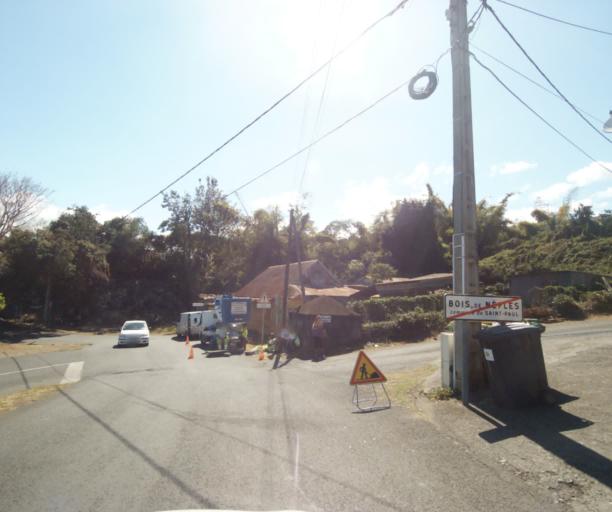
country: RE
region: Reunion
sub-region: Reunion
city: Saint-Paul
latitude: -20.9922
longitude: 55.3270
